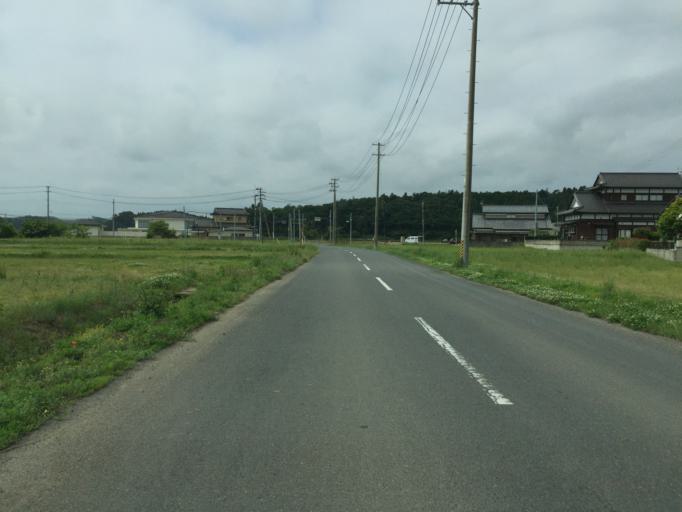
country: JP
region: Fukushima
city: Namie
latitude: 37.6915
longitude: 140.9817
